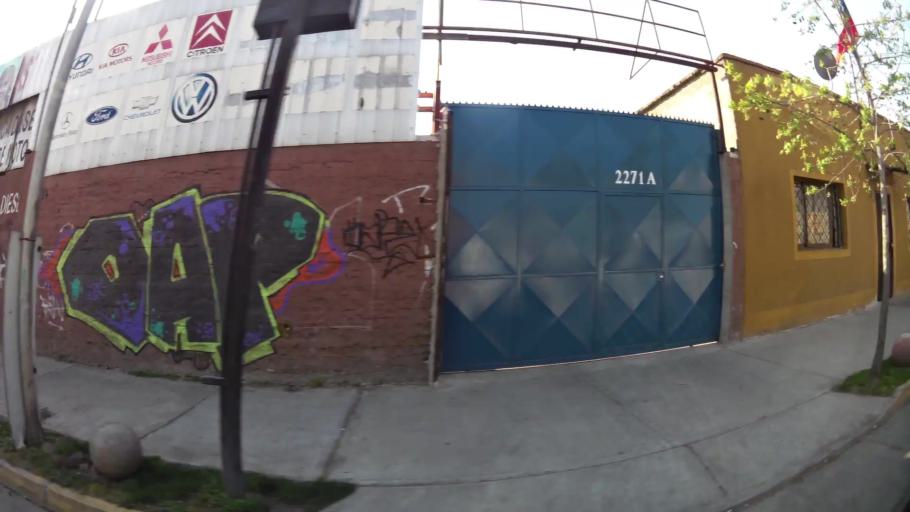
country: CL
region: Santiago Metropolitan
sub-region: Provincia de Santiago
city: Santiago
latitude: -33.4002
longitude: -70.6738
